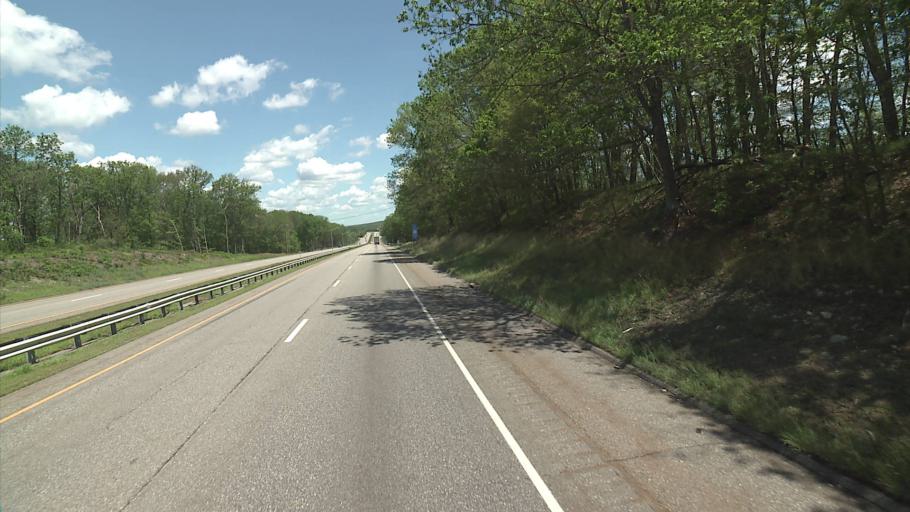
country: US
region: Connecticut
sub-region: Windham County
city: Plainfield Village
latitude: 41.6576
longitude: -71.9224
